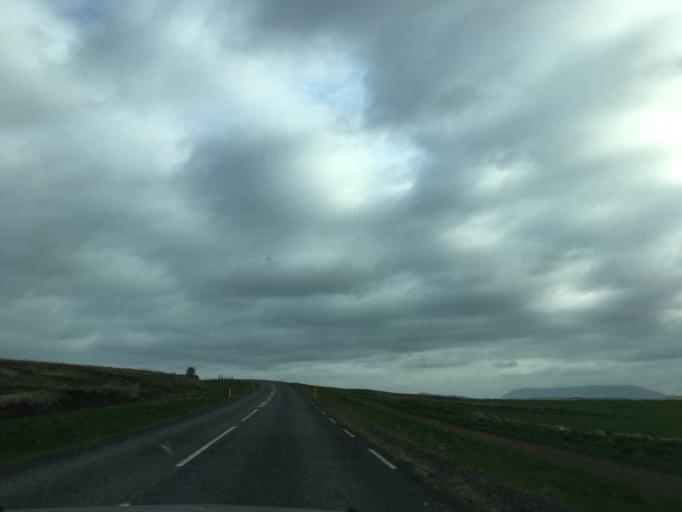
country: IS
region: South
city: Vestmannaeyjar
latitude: 64.1805
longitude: -20.2849
